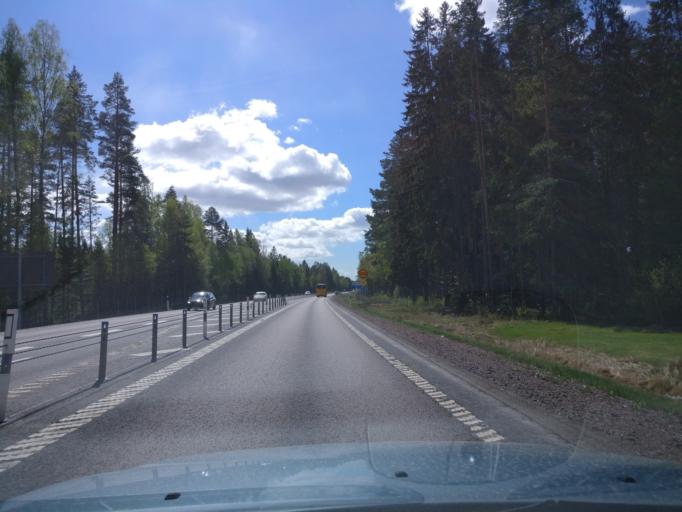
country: SE
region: Vaermland
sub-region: Karlstads Kommun
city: Karlstad
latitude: 59.4366
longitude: 13.5420
